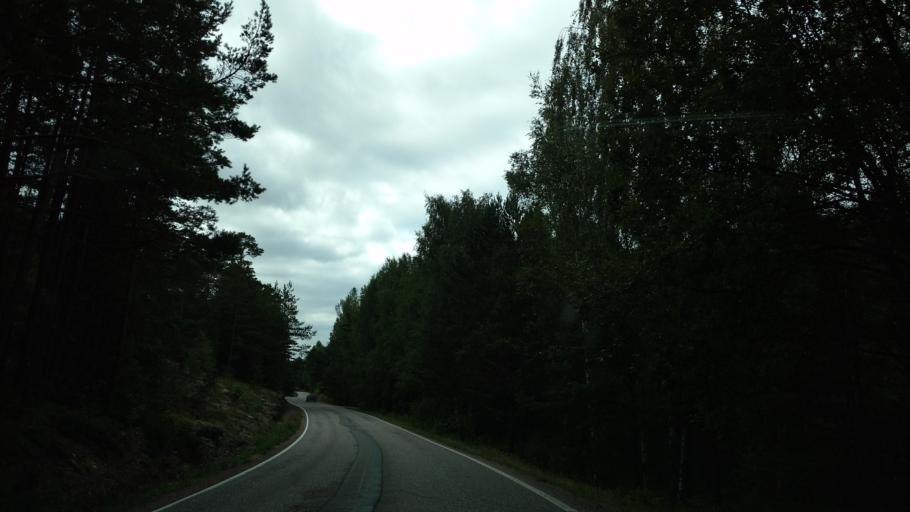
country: FI
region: Varsinais-Suomi
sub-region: Aboland-Turunmaa
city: Dragsfjaerd
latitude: 60.0259
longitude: 22.4596
